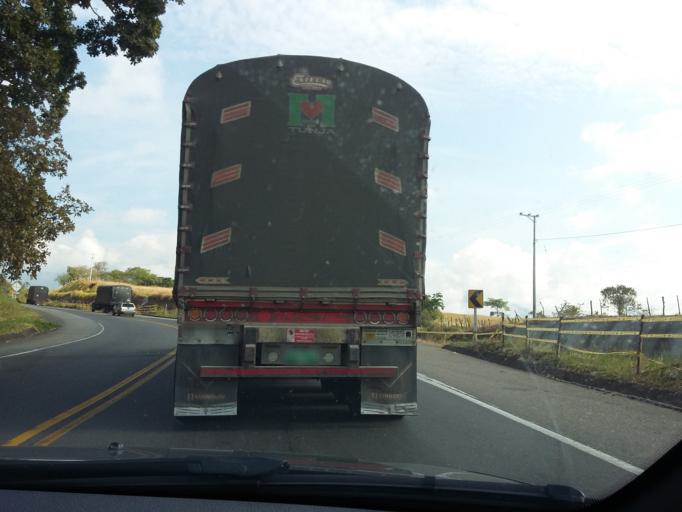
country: CO
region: Tolima
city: Ibague
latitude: 4.4073
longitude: -75.1840
